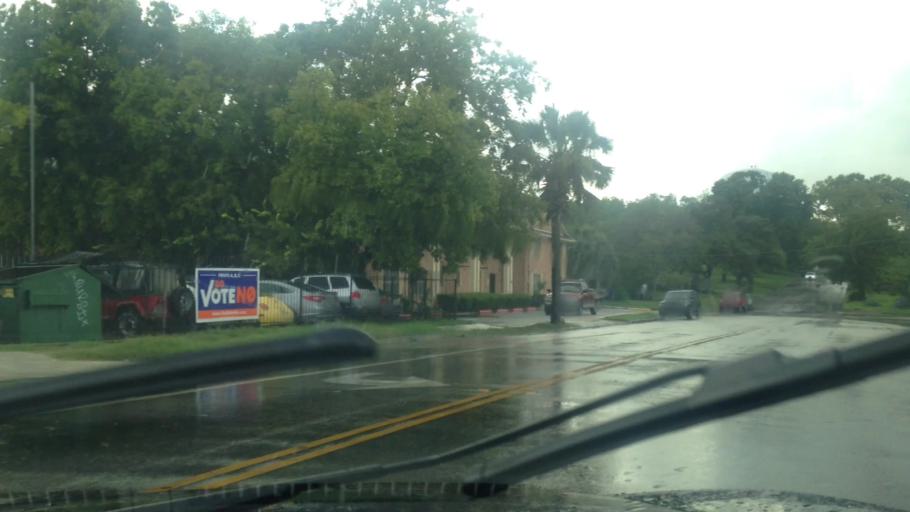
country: US
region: Texas
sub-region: Bexar County
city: Balcones Heights
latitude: 29.4814
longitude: -98.5431
